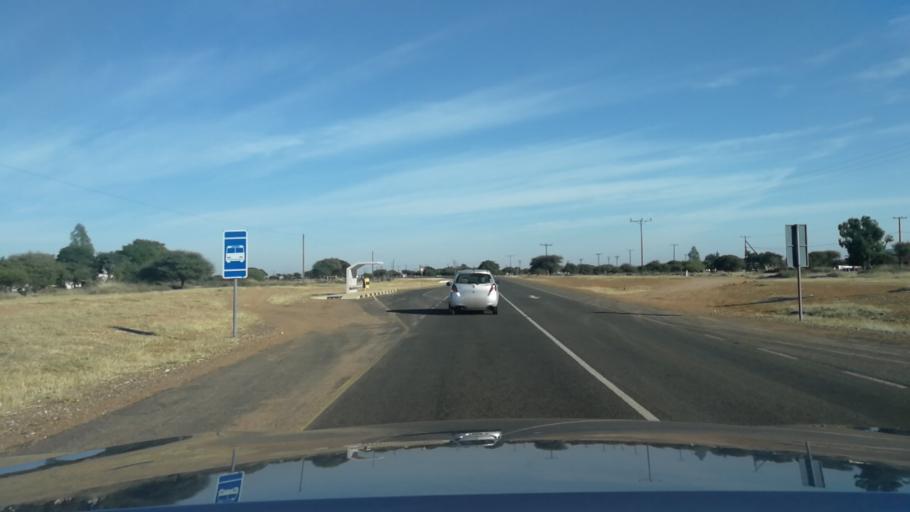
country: BW
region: South East
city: Janeng
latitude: -25.4681
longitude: 25.5460
